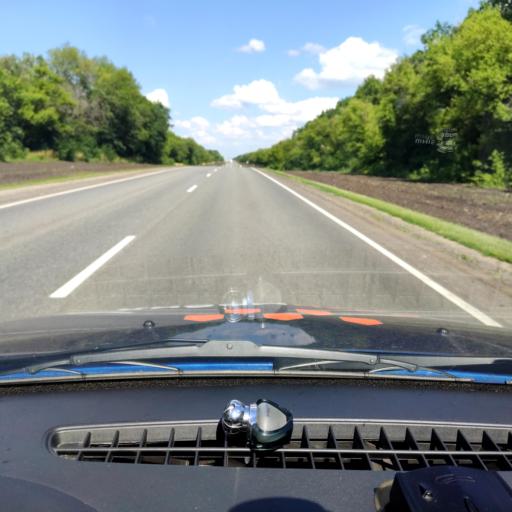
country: RU
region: Orjol
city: Livny
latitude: 52.4330
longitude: 37.8623
